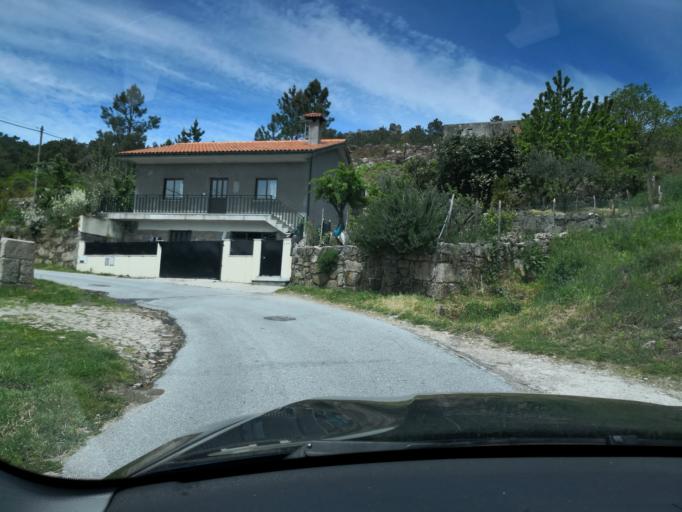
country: PT
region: Vila Real
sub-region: Vila Real
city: Vila Real
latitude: 41.3217
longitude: -7.7913
